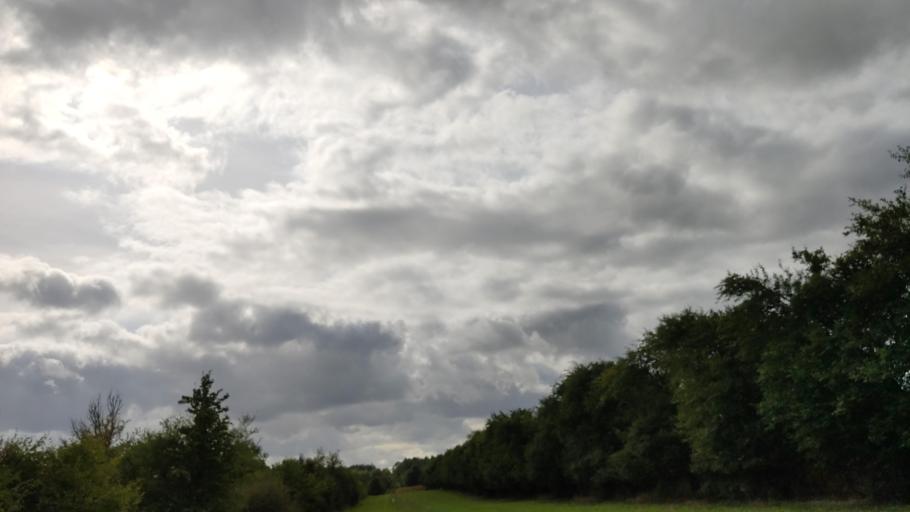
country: PL
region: Kujawsko-Pomorskie
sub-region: Powiat zninski
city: Barcin
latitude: 52.8377
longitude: 17.9511
